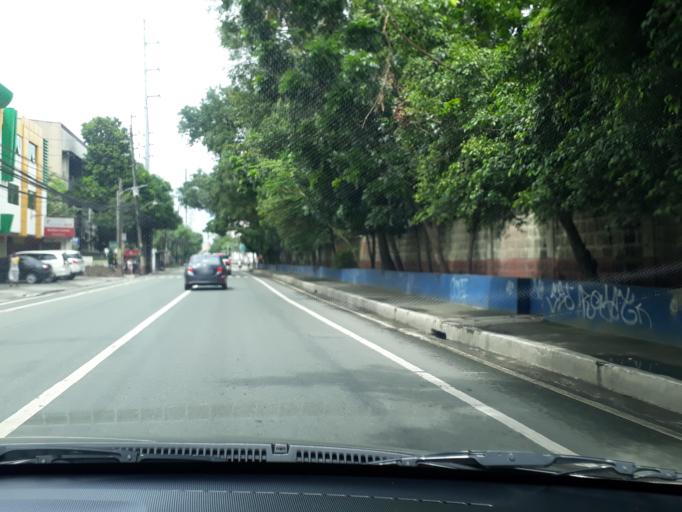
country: PH
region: Metro Manila
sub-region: Pasig
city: Pasig City
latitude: 14.5942
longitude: 121.0879
